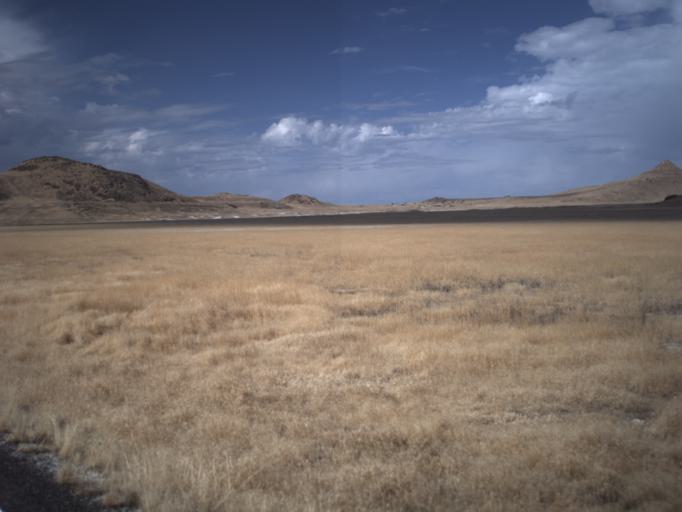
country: US
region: Utah
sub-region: Tooele County
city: Wendover
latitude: 41.3869
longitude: -113.9813
